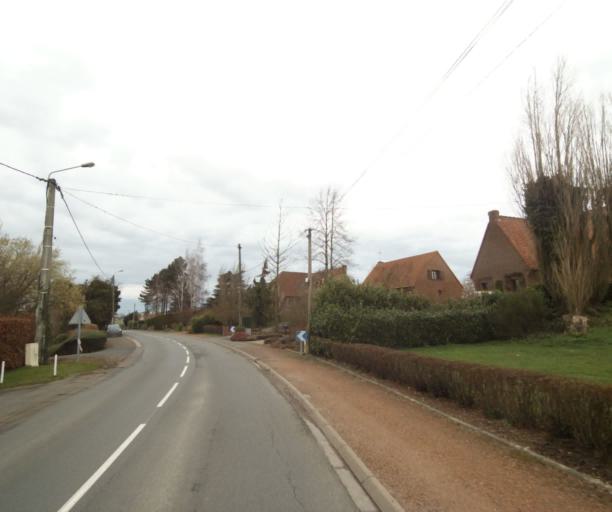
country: FR
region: Nord-Pas-de-Calais
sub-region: Departement du Nord
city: Sebourg
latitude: 50.3325
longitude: 3.6582
